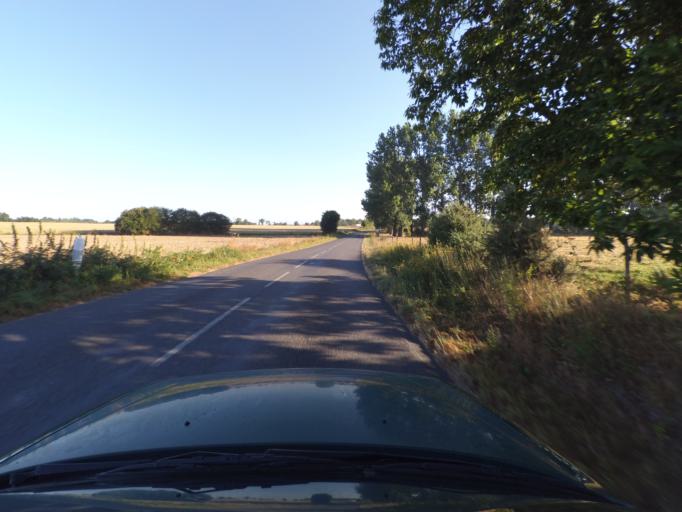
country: FR
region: Pays de la Loire
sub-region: Departement de la Loire-Atlantique
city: Montbert
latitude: 47.0314
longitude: -1.4702
